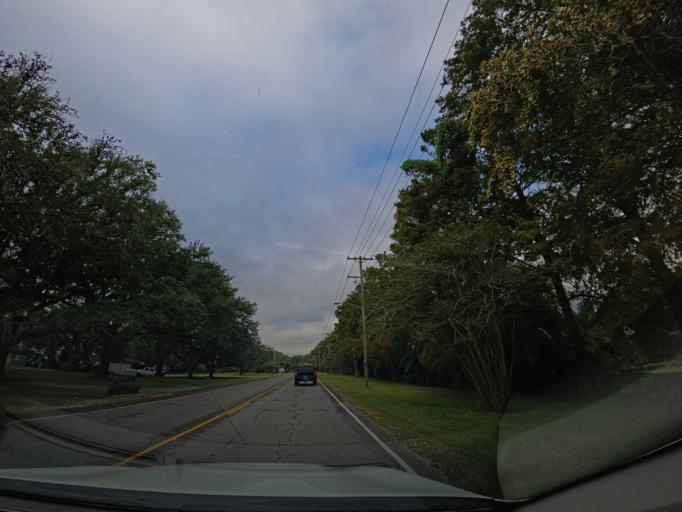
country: US
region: Louisiana
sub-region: Terrebonne Parish
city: Houma
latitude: 29.5755
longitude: -90.7304
